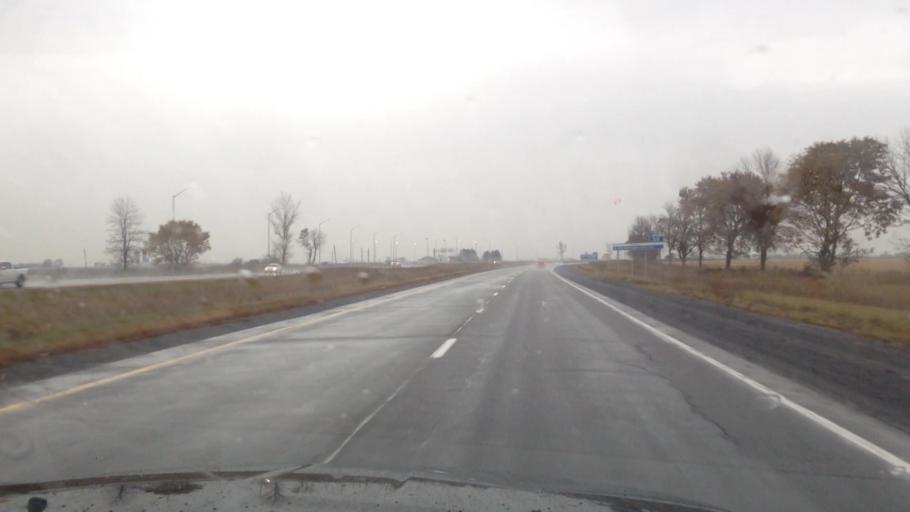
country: CA
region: Ontario
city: Casselman
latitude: 45.3197
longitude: -75.0131
